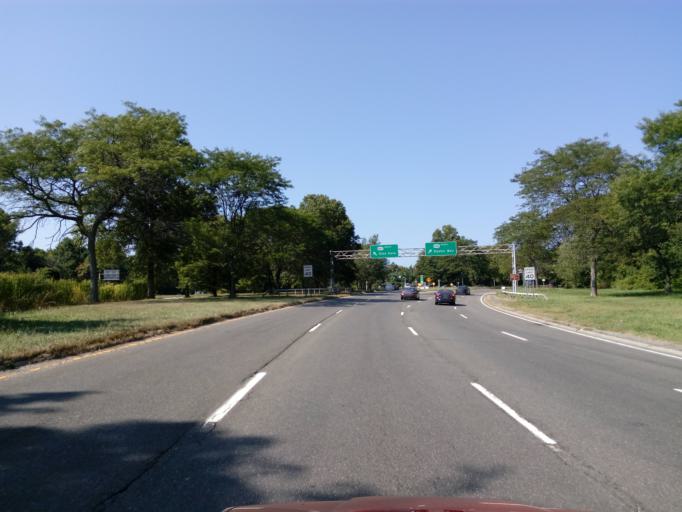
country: US
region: New York
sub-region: Nassau County
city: Jericho
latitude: 40.7931
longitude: -73.5402
